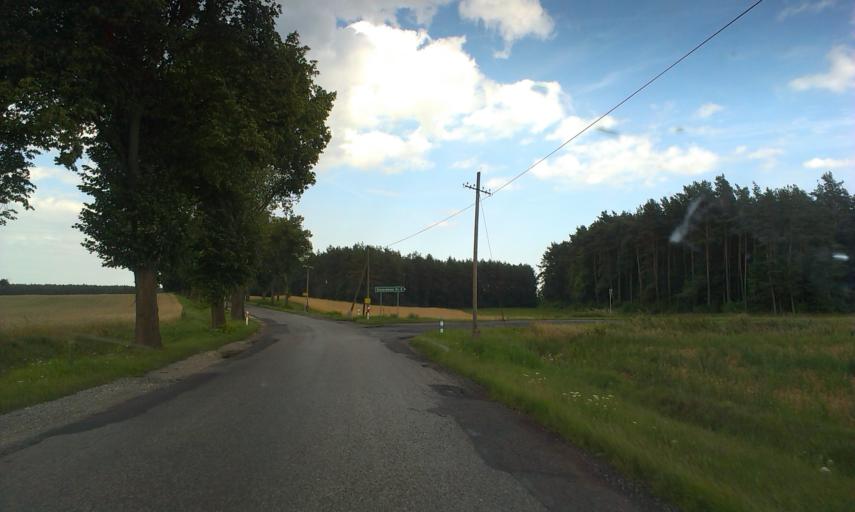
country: PL
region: Greater Poland Voivodeship
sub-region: Powiat zlotowski
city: Krajenka
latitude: 53.2871
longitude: 17.0032
